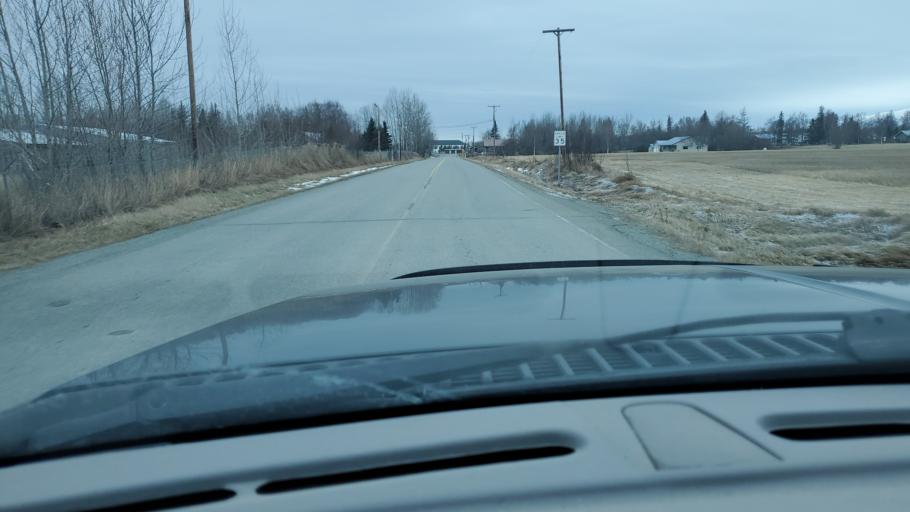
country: US
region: Alaska
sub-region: Matanuska-Susitna Borough
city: Palmer
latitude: 61.5994
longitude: -149.0953
